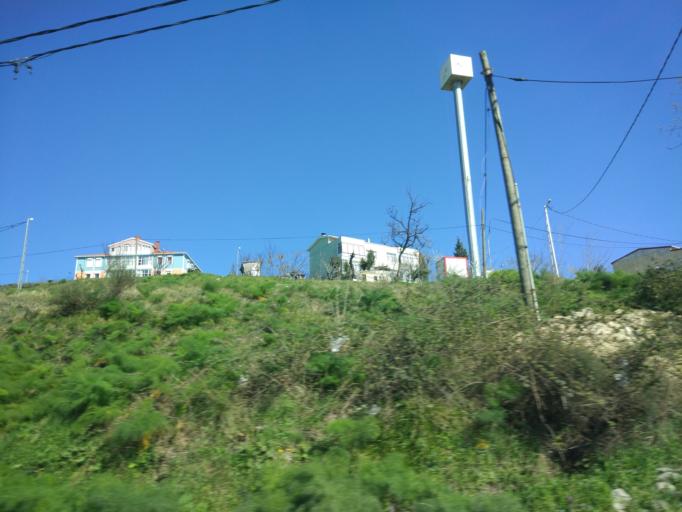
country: TR
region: Istanbul
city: Basaksehir
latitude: 41.0476
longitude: 28.7487
